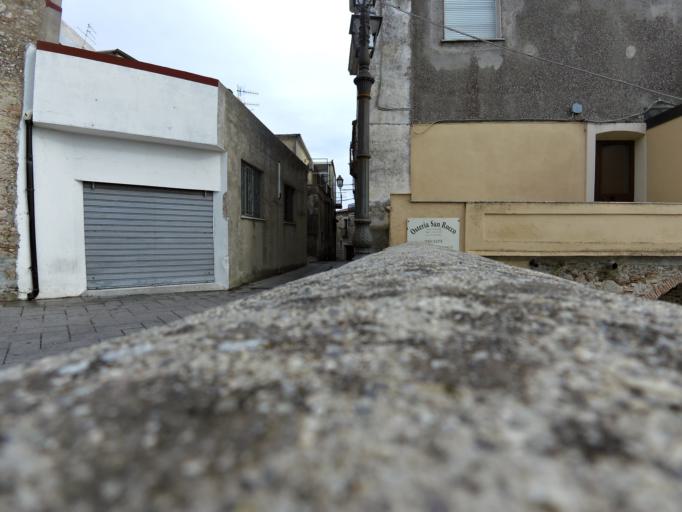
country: IT
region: Calabria
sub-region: Provincia di Reggio Calabria
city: Stignano
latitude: 38.4177
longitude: 16.4702
